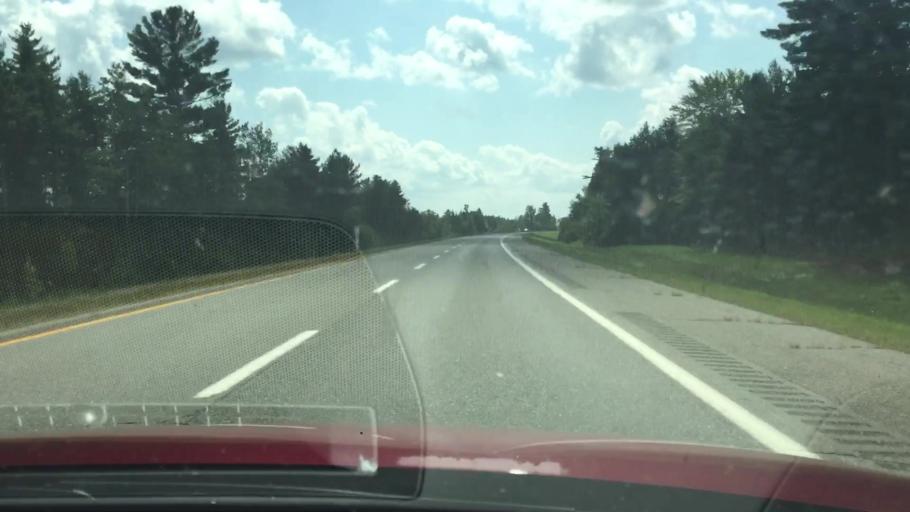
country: US
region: Maine
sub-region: Penobscot County
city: Medway
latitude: 45.5064
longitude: -68.5555
